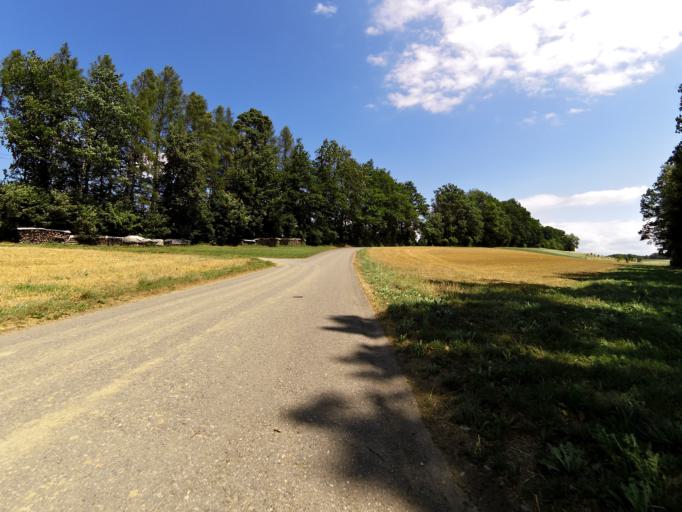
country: CH
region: Thurgau
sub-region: Weinfelden District
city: Maerstetten-Dorf
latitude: 47.6041
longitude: 9.0597
